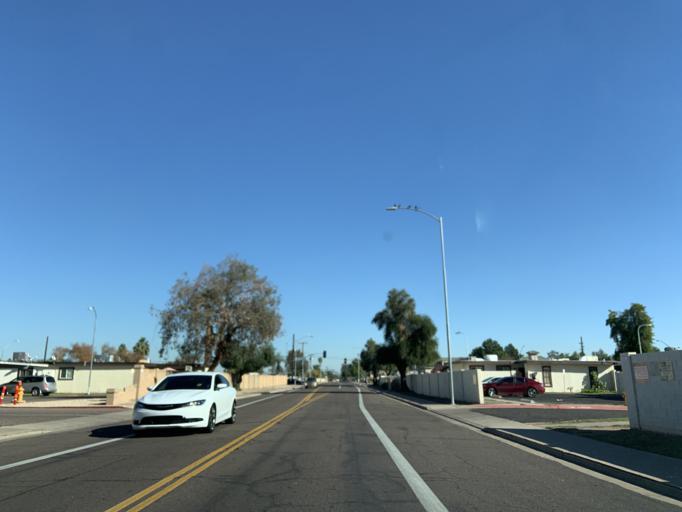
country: US
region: Arizona
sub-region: Maricopa County
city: Tempe
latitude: 33.4003
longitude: -111.8761
